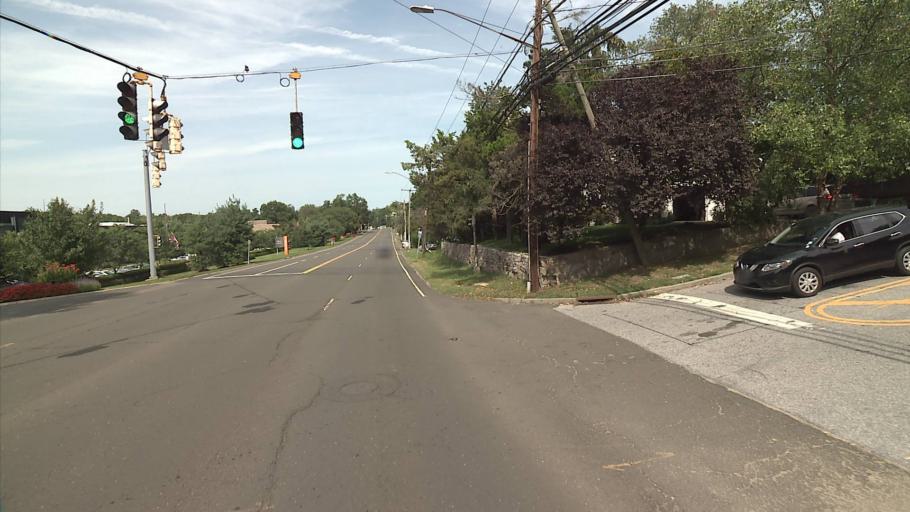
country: US
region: Connecticut
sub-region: Fairfield County
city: Stamford
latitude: 41.0787
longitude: -73.5535
